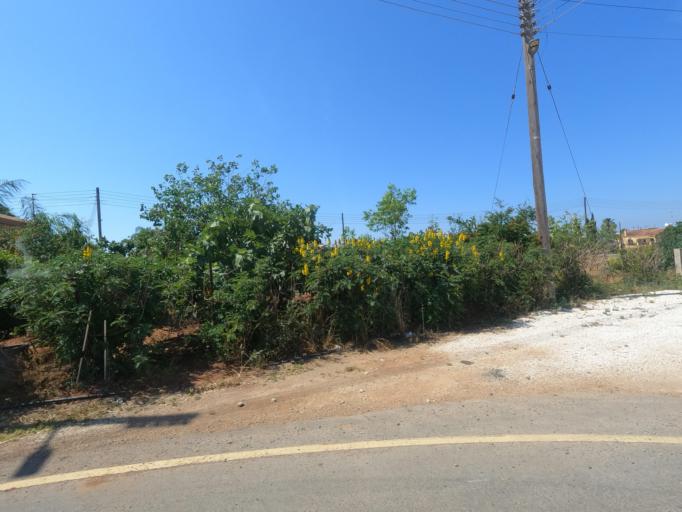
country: CY
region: Ammochostos
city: Liopetri
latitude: 35.0146
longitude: 33.8899
